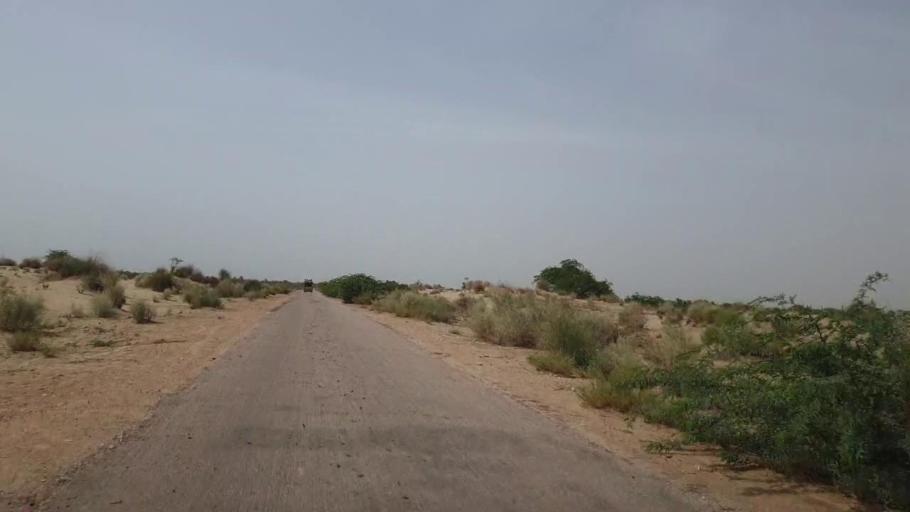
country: PK
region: Sindh
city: Bandhi
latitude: 26.5615
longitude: 68.3817
